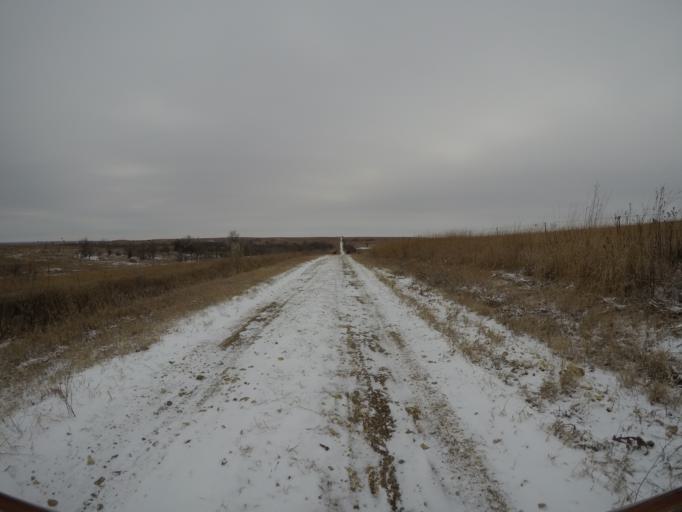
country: US
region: Kansas
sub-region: Wabaunsee County
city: Alma
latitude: 38.8725
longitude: -96.1136
